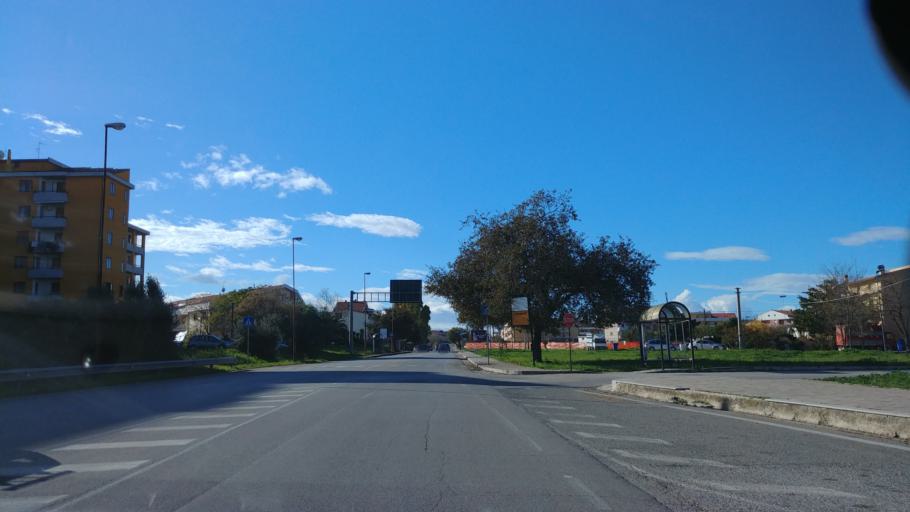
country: IT
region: Molise
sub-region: Provincia di Campobasso
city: Termoli
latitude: 41.9934
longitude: 14.9787
